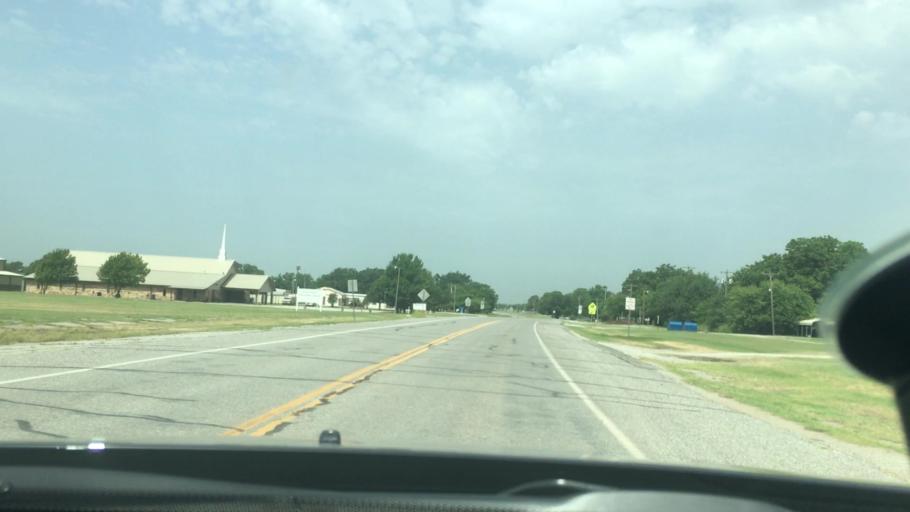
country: US
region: Oklahoma
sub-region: Garvin County
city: Pauls Valley
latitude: 34.8259
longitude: -97.2606
